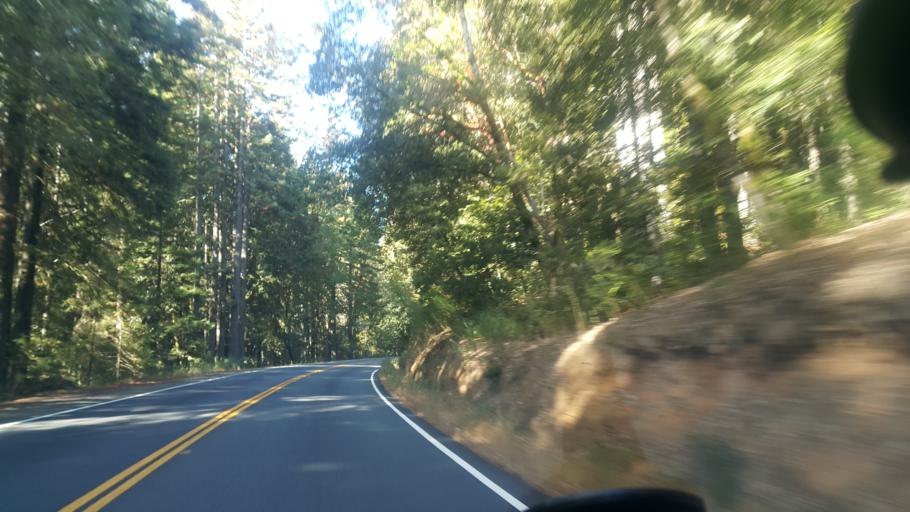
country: US
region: California
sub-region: Mendocino County
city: Fort Bragg
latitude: 39.3631
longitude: -123.6667
